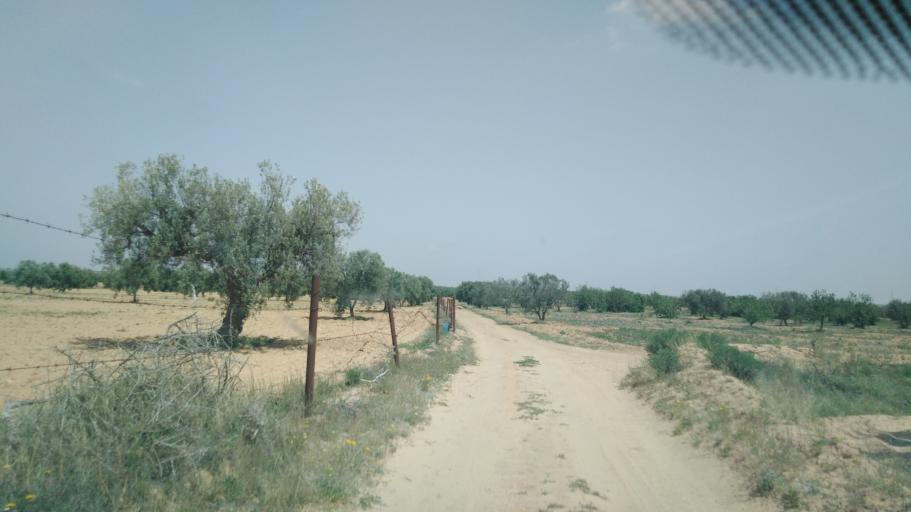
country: TN
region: Safaqis
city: Sfax
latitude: 34.7325
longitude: 10.5746
